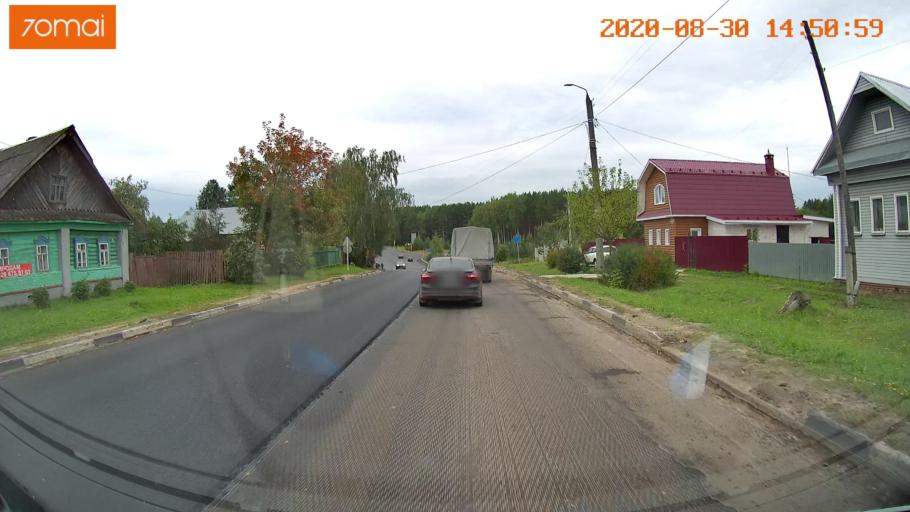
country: RU
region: Ivanovo
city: Kineshma
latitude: 57.4266
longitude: 42.0900
